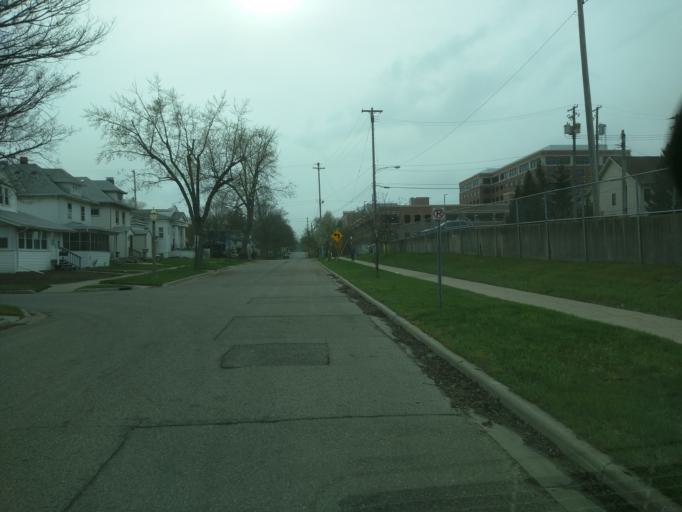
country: US
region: Michigan
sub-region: Ingham County
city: Lansing
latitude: 42.7323
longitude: -84.5317
